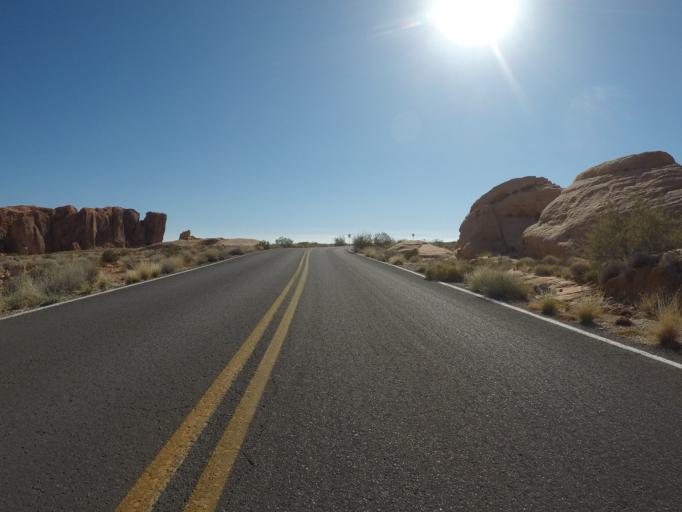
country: US
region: Nevada
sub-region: Clark County
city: Moapa Valley
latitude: 36.4903
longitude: -114.5296
